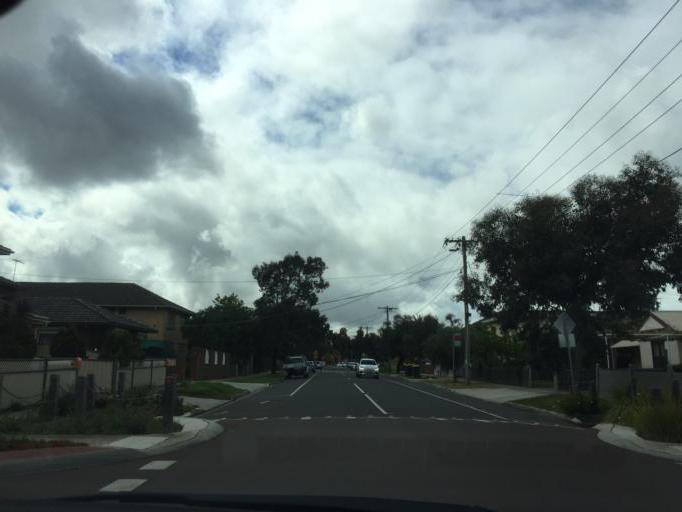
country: AU
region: Victoria
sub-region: Brimbank
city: Sunshine West
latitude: -37.7837
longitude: 144.8245
